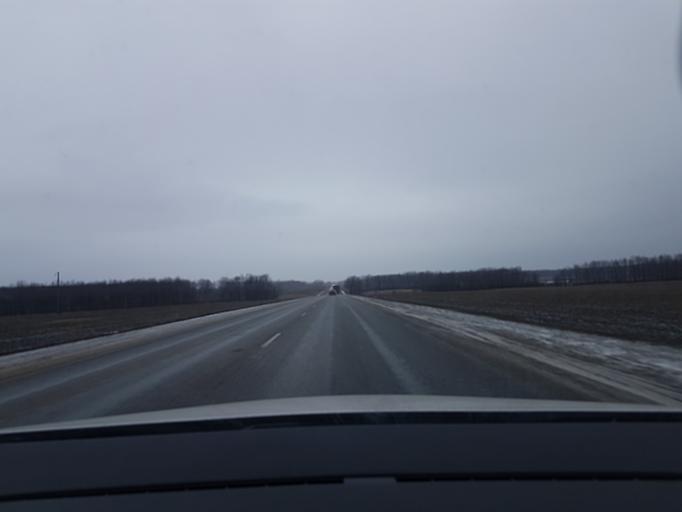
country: RU
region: Tambov
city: Zavoronezhskoye
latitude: 52.9934
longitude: 40.5526
